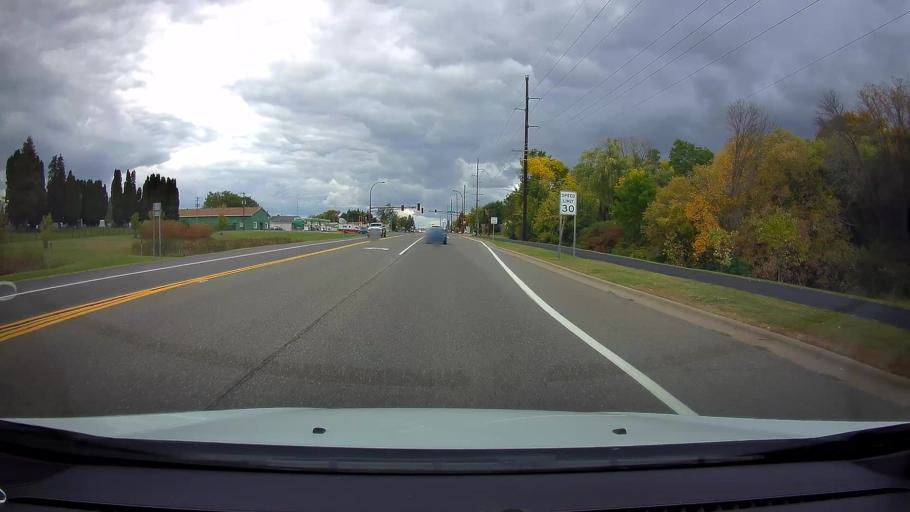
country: US
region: Minnesota
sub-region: Chisago County
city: Lindstrom
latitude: 45.3910
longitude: -92.8342
